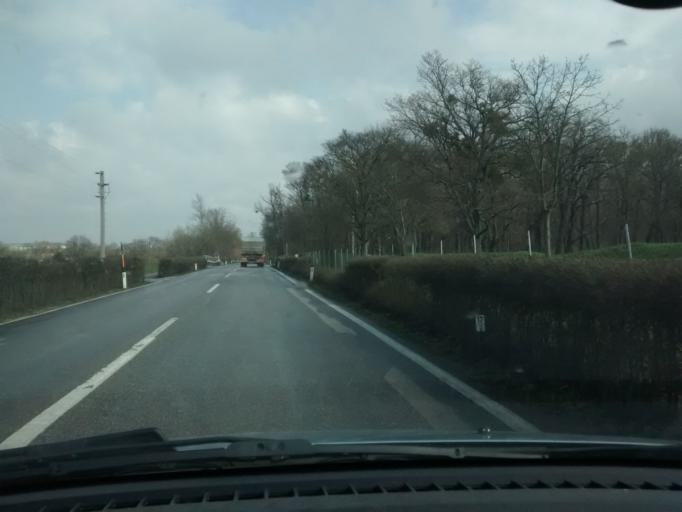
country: AT
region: Lower Austria
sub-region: Politischer Bezirk Modling
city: Laxenburg
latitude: 48.0600
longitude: 16.3528
